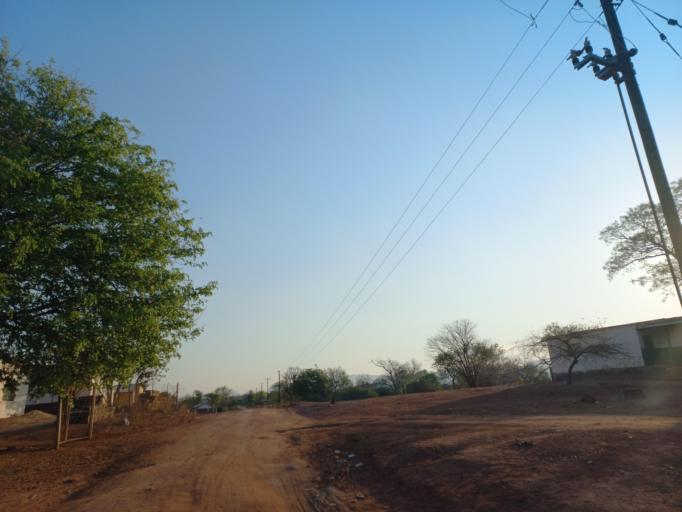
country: ZM
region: Lusaka
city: Luangwa
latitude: -15.6136
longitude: 30.3917
